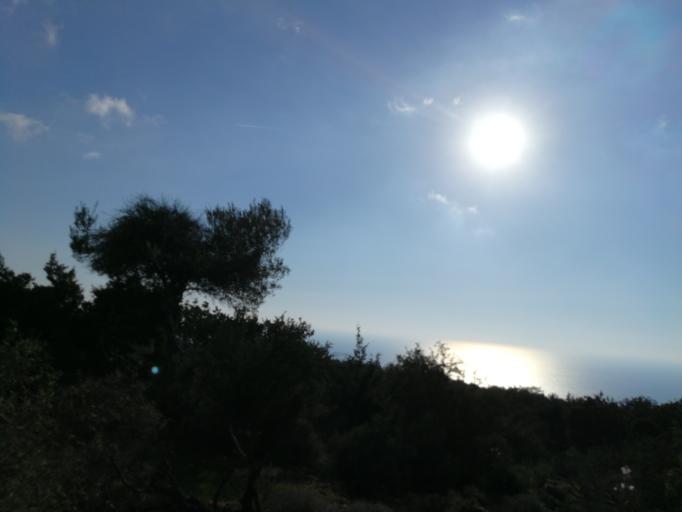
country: CY
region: Pafos
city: Pegeia
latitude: 34.9254
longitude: 32.3543
